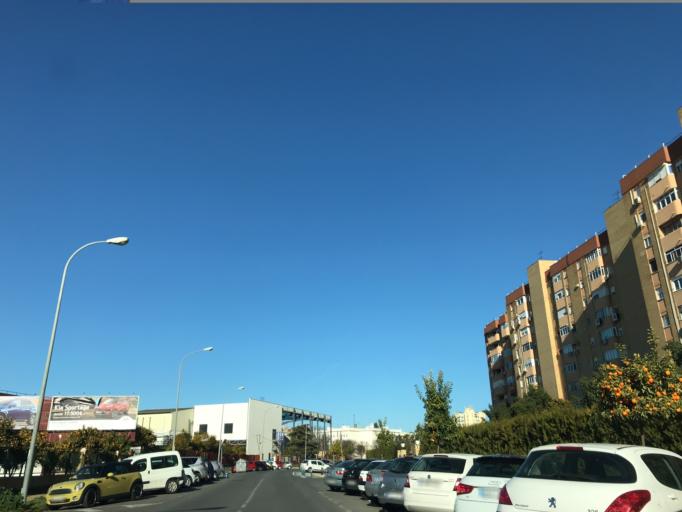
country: ES
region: Andalusia
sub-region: Provincia de Sevilla
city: Sevilla
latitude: 37.3952
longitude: -5.9545
